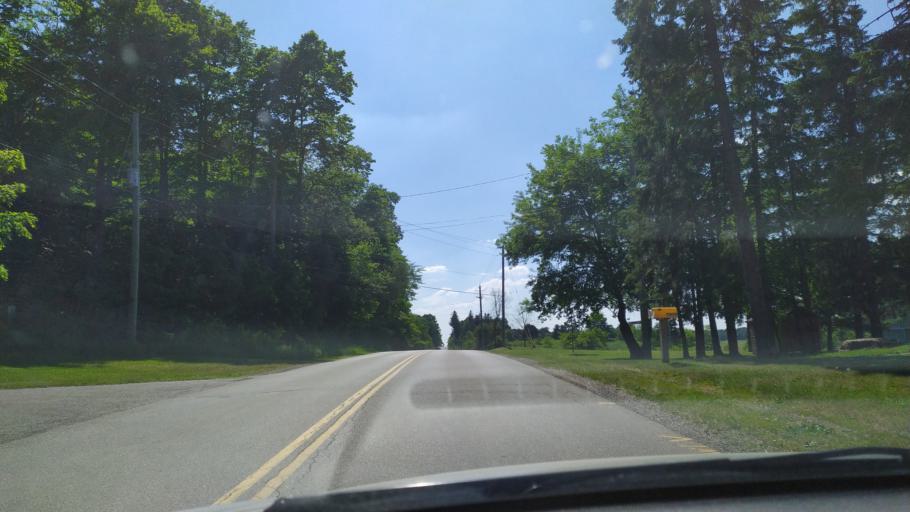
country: CA
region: Ontario
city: Kitchener
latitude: 43.3693
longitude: -80.5710
